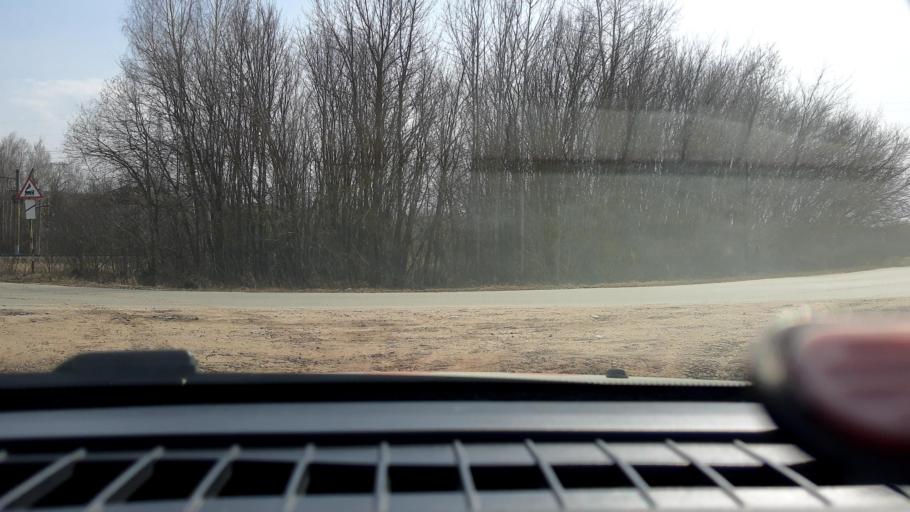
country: RU
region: Nizjnij Novgorod
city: Burevestnik
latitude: 56.0407
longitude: 43.8452
